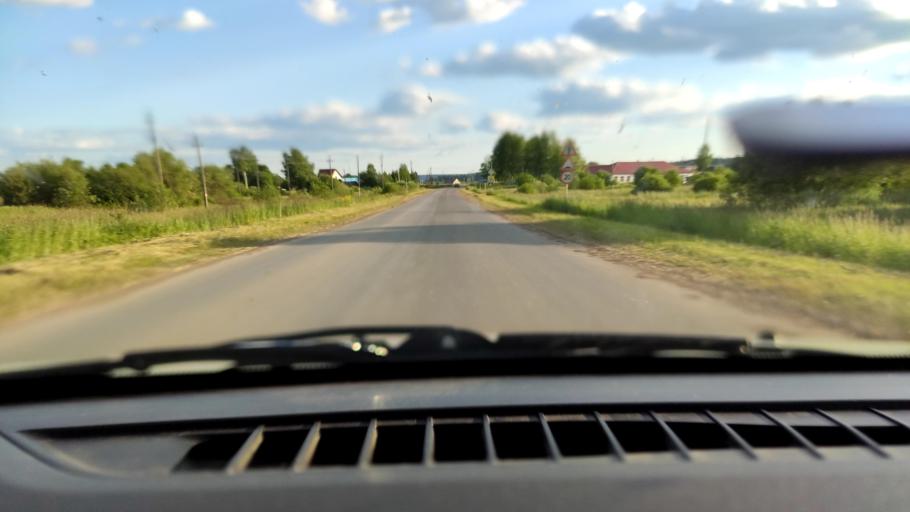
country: RU
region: Perm
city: Uinskoye
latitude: 57.0965
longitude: 56.6428
